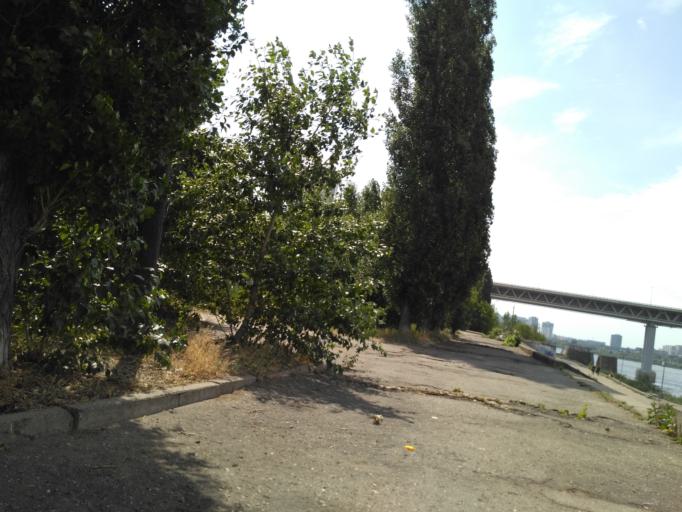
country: RU
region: Nizjnij Novgorod
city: Nizhniy Novgorod
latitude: 56.3204
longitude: 43.9724
